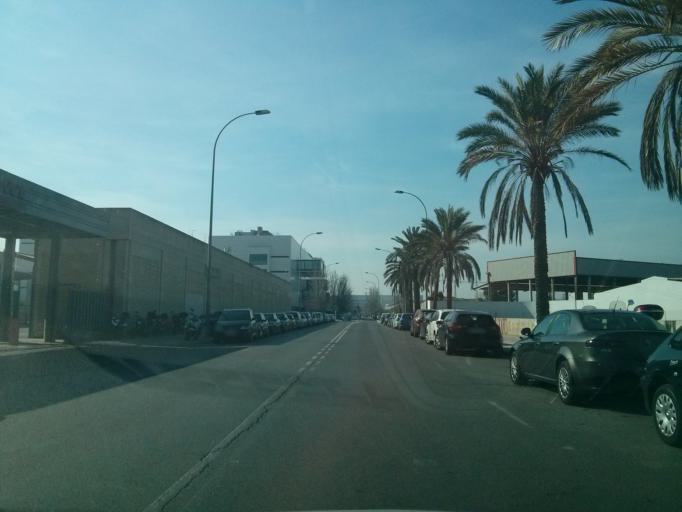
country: ES
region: Valencia
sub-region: Provincia de Valencia
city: Alboraya
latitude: 39.4813
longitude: -0.3350
